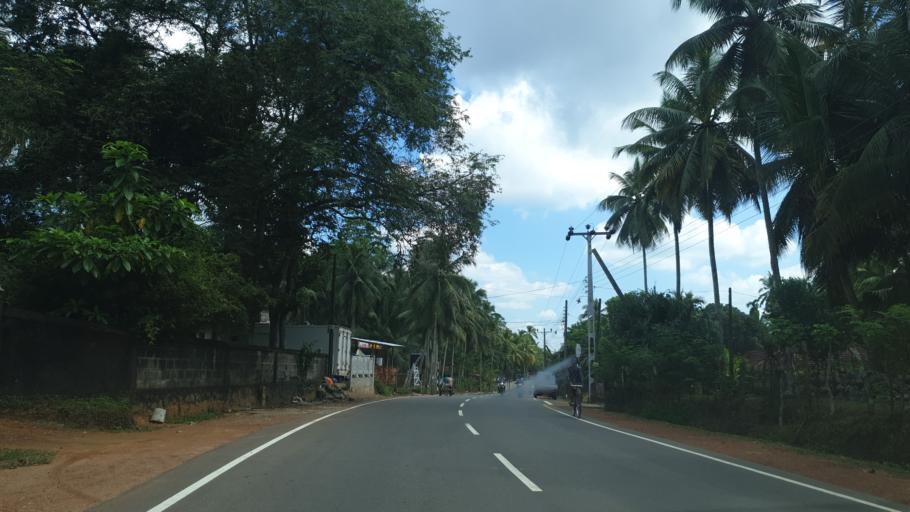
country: LK
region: Western
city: Panadura
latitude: 6.6651
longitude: 79.9540
